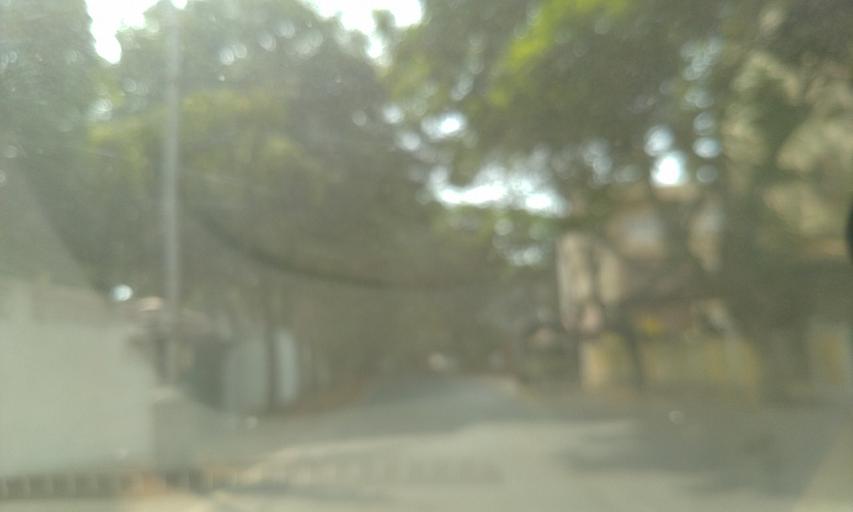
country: IN
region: Goa
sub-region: North Goa
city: Panaji
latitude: 15.4911
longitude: 73.8241
